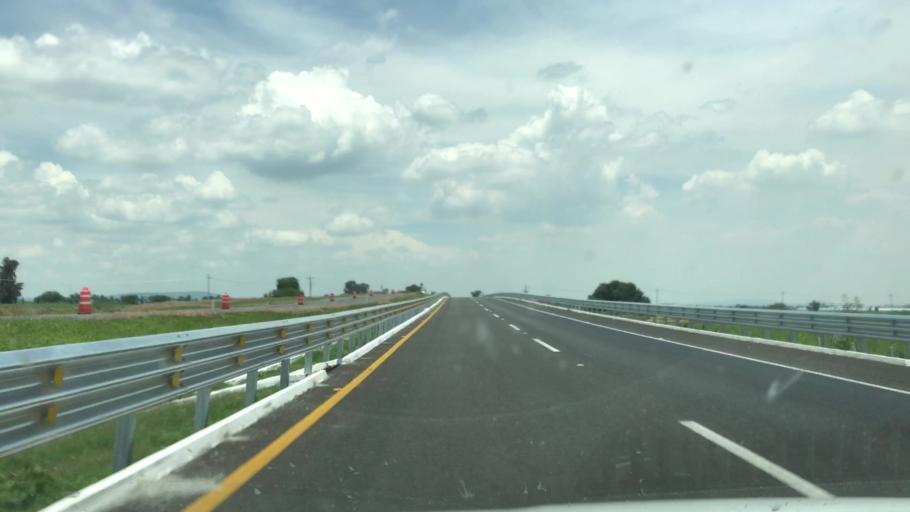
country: MX
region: Guanajuato
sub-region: Irapuato
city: Cuarta Brigada
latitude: 20.6464
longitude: -101.2760
